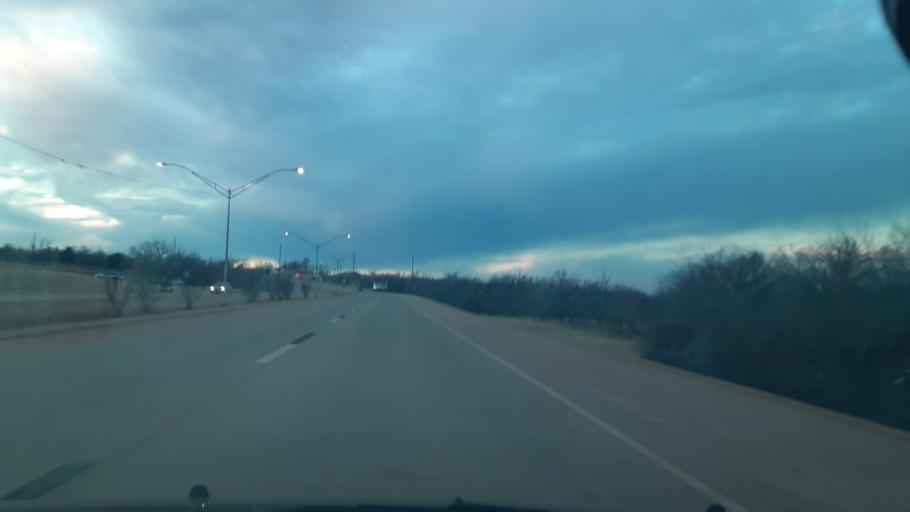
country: US
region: Oklahoma
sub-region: Logan County
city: Guthrie
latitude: 35.8793
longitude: -97.4021
